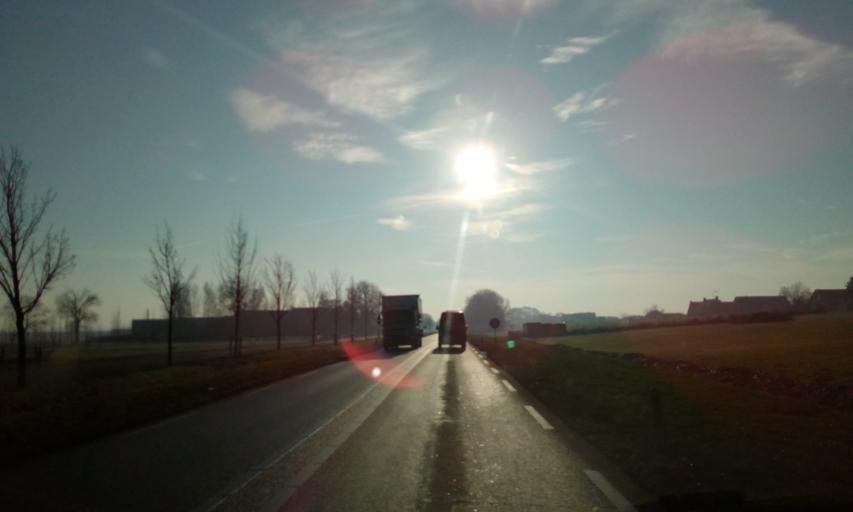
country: NL
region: South Holland
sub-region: Gemeente Lansingerland
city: Bleiswijk
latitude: 51.9964
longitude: 4.5940
